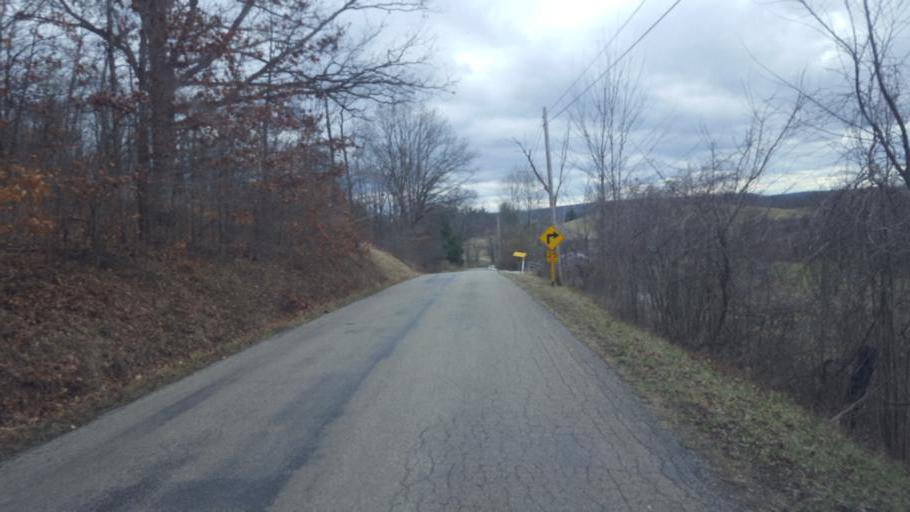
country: US
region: Ohio
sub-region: Muskingum County
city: Frazeysburg
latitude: 40.0994
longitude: -82.2024
